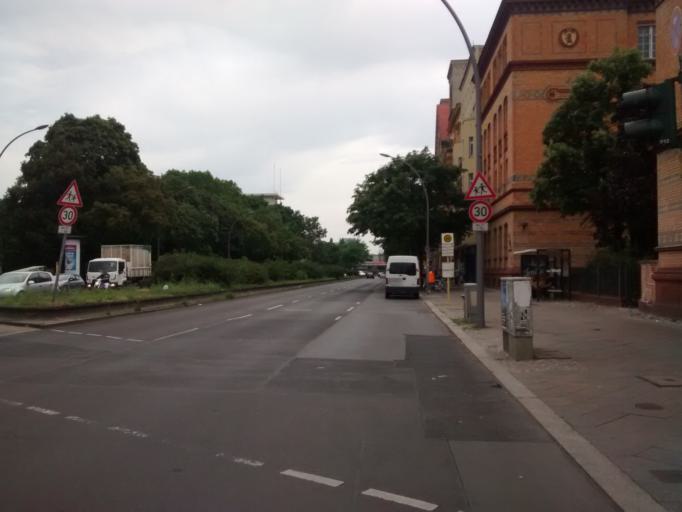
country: DE
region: Berlin
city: Wedding Bezirk
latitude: 52.5447
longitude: 13.3619
